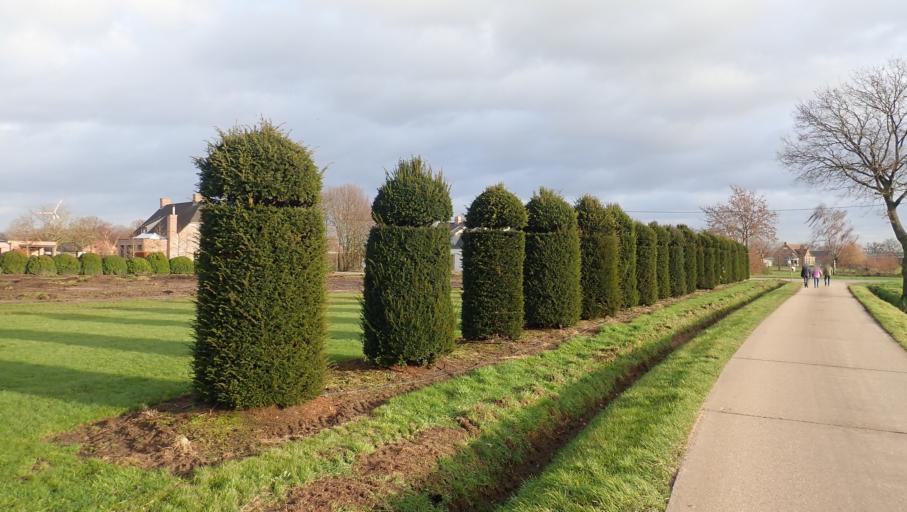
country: BE
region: Flanders
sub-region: Provincie Antwerpen
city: Brecht
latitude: 51.3629
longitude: 4.6324
